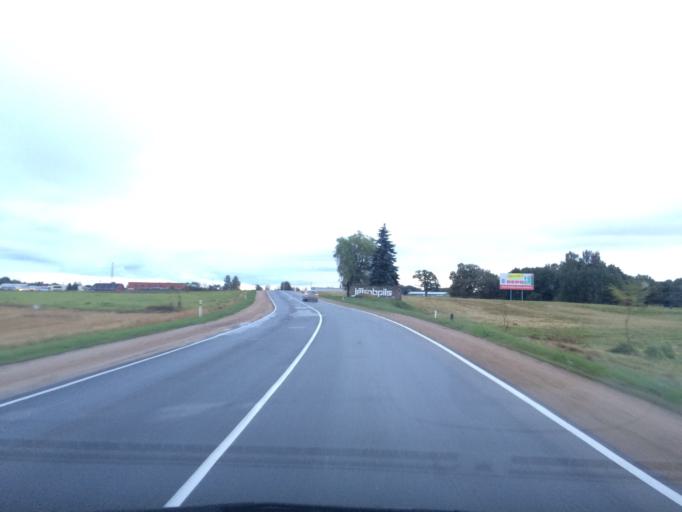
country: LV
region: Jekabpils Rajons
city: Jekabpils
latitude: 56.5245
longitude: 25.8364
